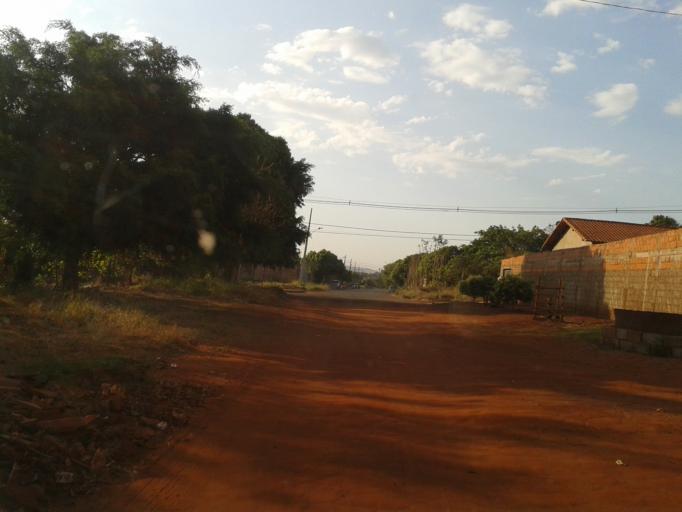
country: BR
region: Minas Gerais
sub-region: Ituiutaba
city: Ituiutaba
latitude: -18.9961
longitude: -49.4372
